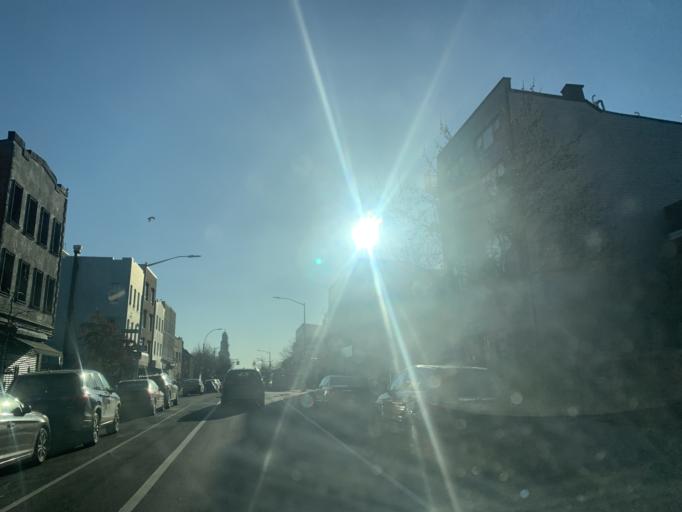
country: US
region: New York
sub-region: Kings County
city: East New York
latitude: 40.6975
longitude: -73.9242
